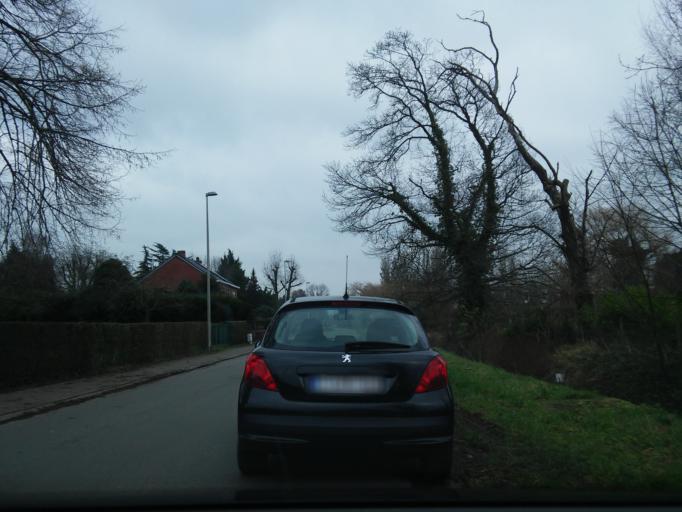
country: BE
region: Flanders
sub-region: Provincie Oost-Vlaanderen
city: Wetteren
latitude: 51.0115
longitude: 3.8855
